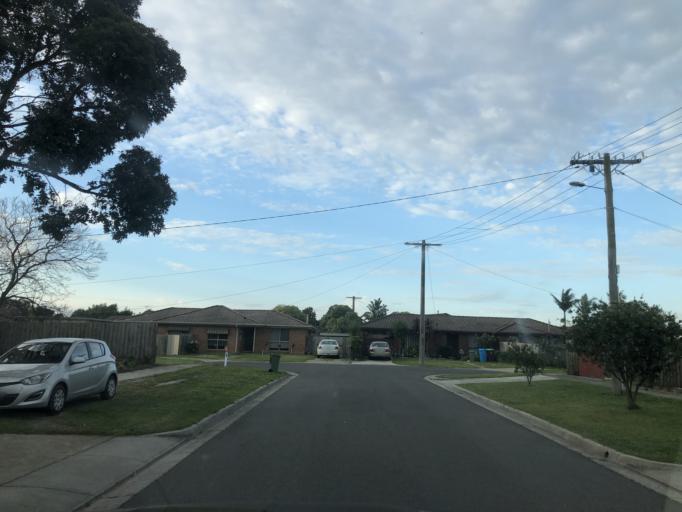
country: AU
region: Victoria
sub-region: Casey
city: Hampton Park
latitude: -38.0287
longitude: 145.2533
